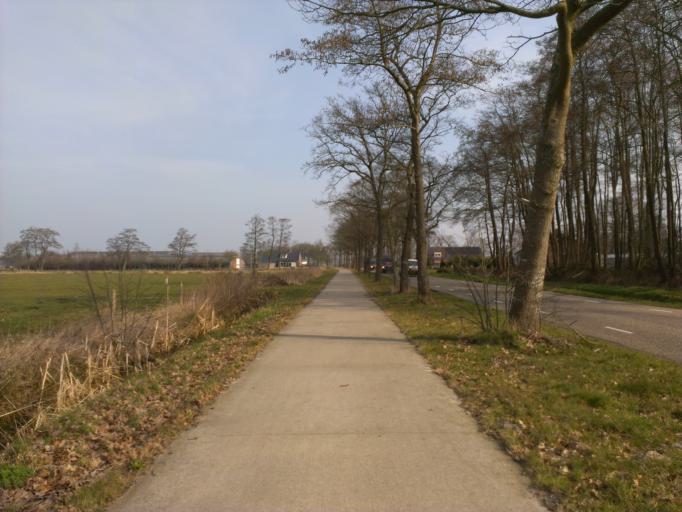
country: NL
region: Drenthe
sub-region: Gemeente Hoogeveen
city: Hoogeveen
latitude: 52.7409
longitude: 6.4917
